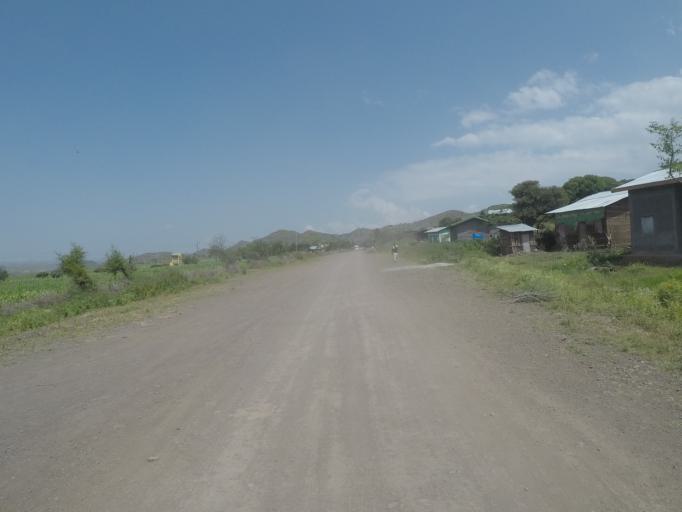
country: ET
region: Amhara
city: Lalibela
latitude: 11.9802
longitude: 38.9871
